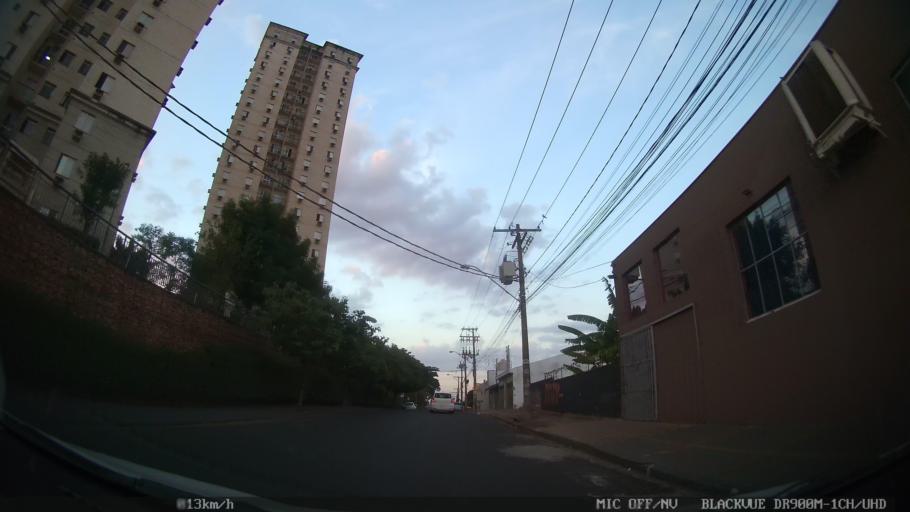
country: BR
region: Sao Paulo
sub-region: Ribeirao Preto
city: Ribeirao Preto
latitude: -21.1562
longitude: -47.8287
